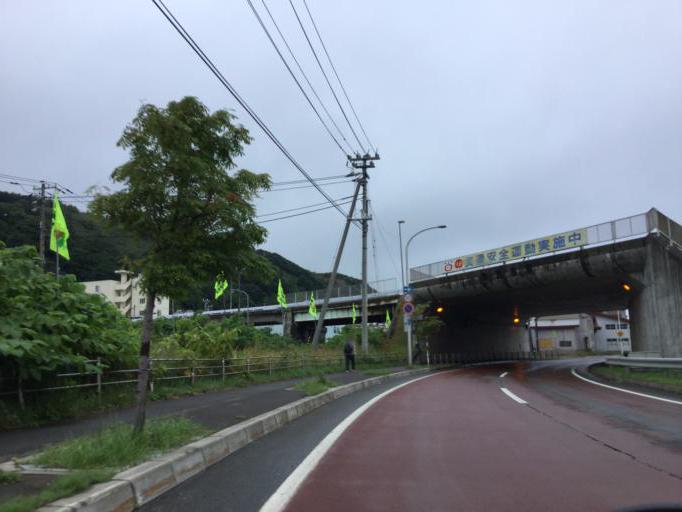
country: JP
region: Hokkaido
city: Wakkanai
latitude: 45.4049
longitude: 141.6754
